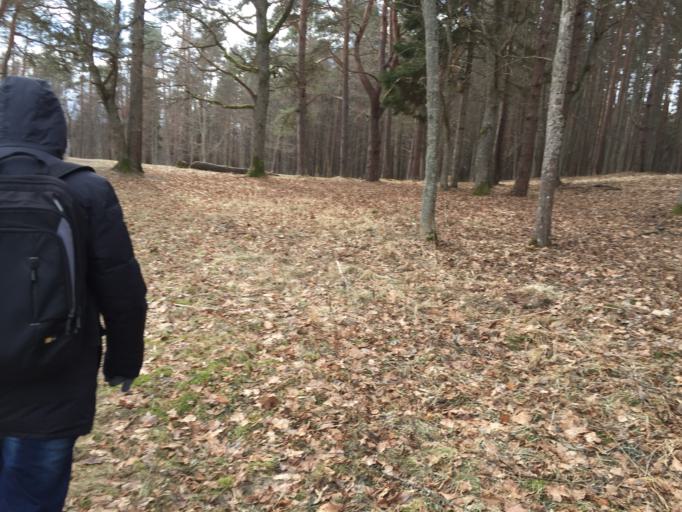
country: LV
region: Valmieras Rajons
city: Valmiera
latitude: 57.5377
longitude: 25.4443
